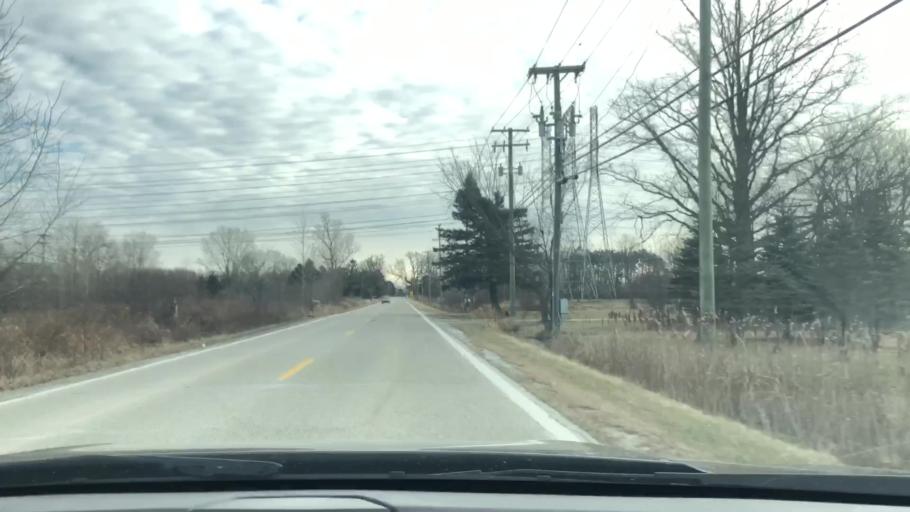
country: US
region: Michigan
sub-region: Macomb County
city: Shelby
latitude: 42.7289
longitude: -83.0100
